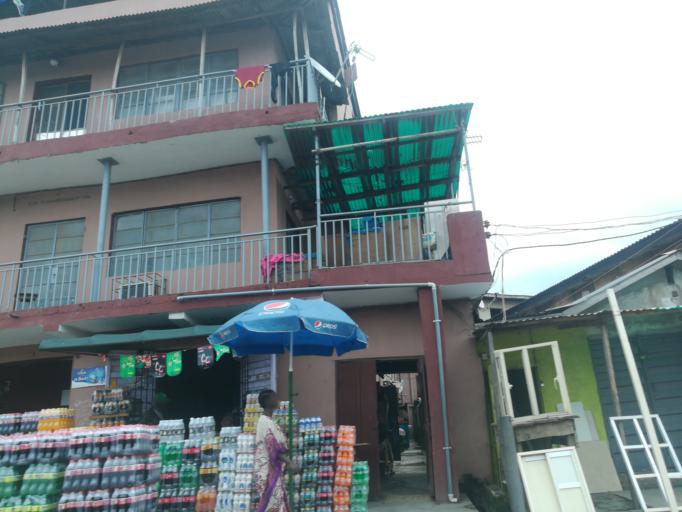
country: NG
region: Lagos
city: Mushin
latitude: 6.5317
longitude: 3.3576
